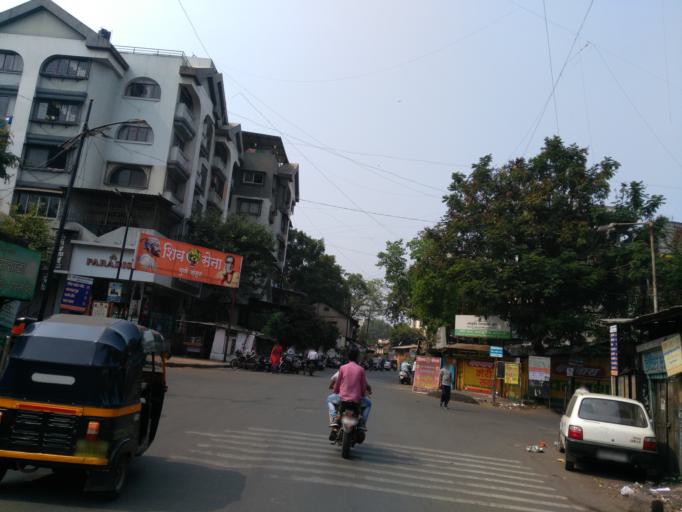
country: IN
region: Maharashtra
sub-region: Pune Division
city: Pune
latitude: 18.5195
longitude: 73.8644
